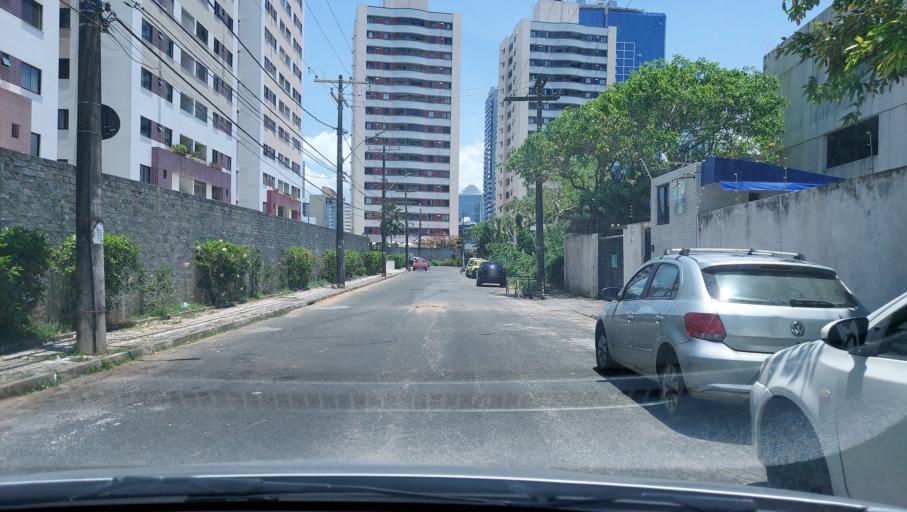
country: BR
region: Bahia
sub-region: Salvador
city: Salvador
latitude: -12.9816
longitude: -38.4482
